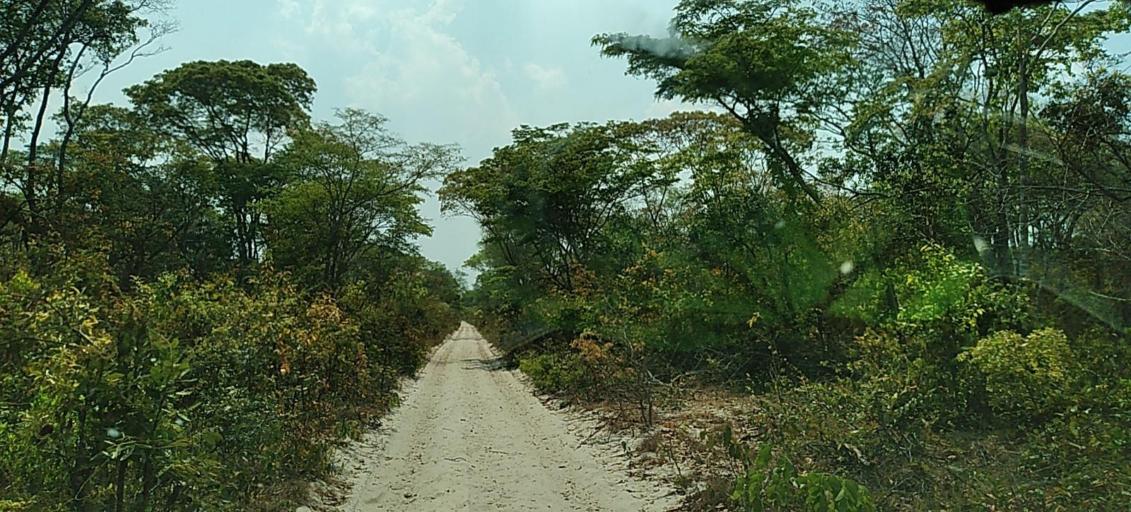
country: ZM
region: North-Western
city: Kabompo
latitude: -13.3966
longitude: 23.8007
